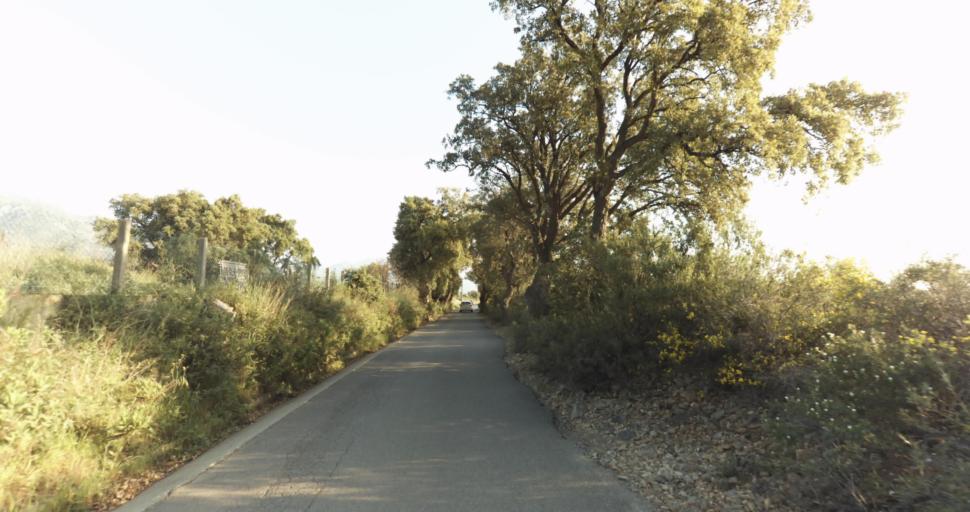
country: FR
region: Corsica
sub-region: Departement de la Haute-Corse
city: Biguglia
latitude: 42.6050
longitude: 9.4443
